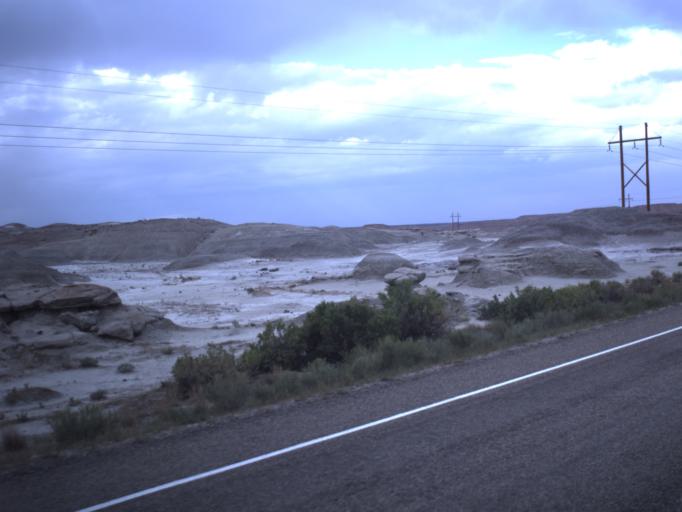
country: US
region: Colorado
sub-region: Rio Blanco County
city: Rangely
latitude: 40.1001
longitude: -109.2268
